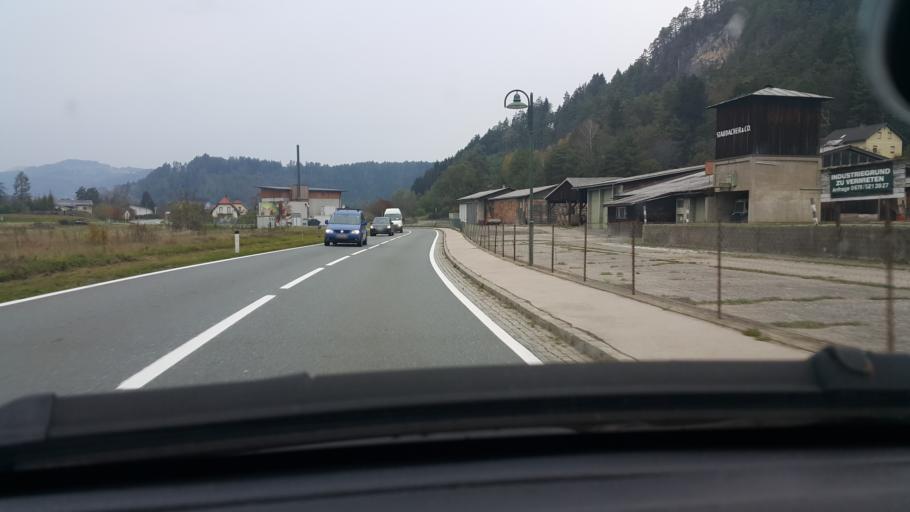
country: AT
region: Carinthia
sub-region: Politischer Bezirk Wolfsberg
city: Lavamund
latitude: 46.6384
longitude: 14.9529
